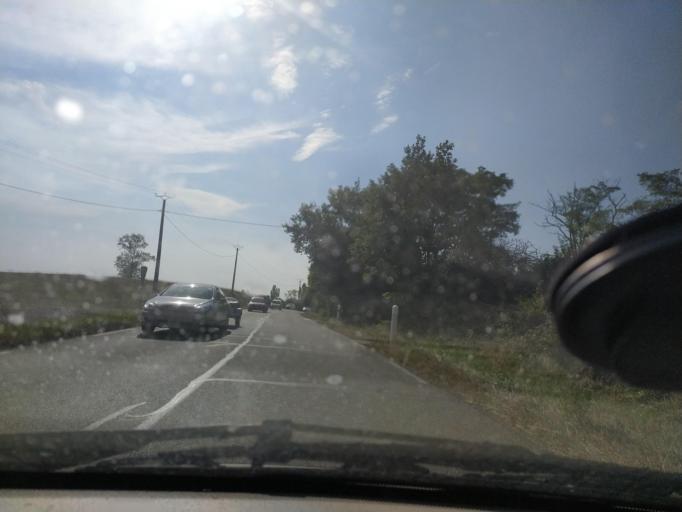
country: FR
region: Midi-Pyrenees
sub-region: Departement du Gers
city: Eauze
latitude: 43.7946
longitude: 0.0824
